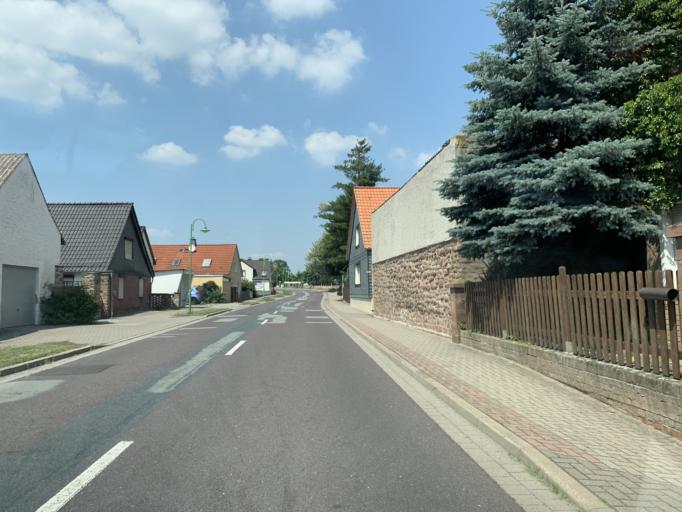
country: DE
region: Saxony-Anhalt
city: Erxleben
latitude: 52.2028
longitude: 11.2610
